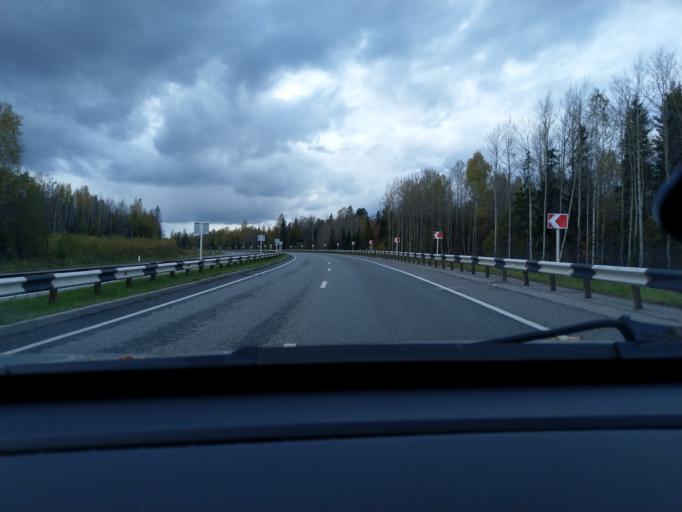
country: RU
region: Perm
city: Polazna
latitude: 58.3362
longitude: 56.4788
